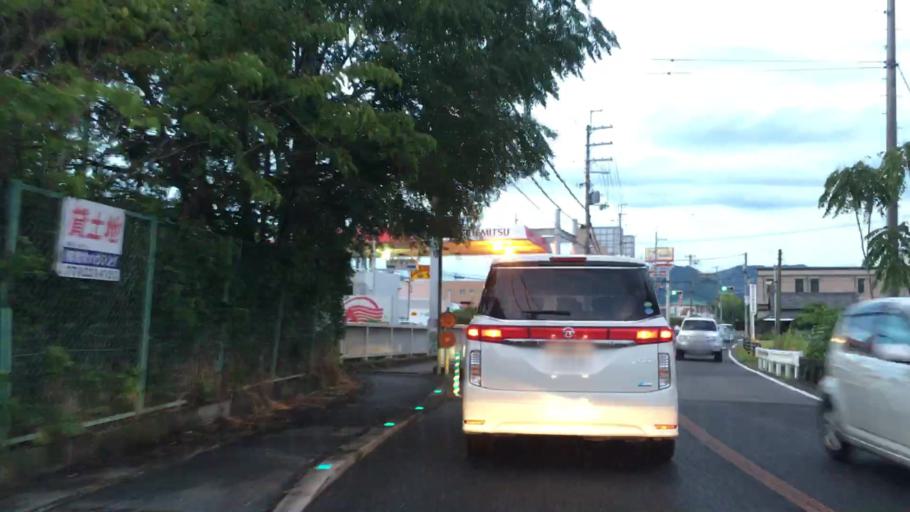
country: JP
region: Hyogo
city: Himeji
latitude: 34.9406
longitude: 134.7445
